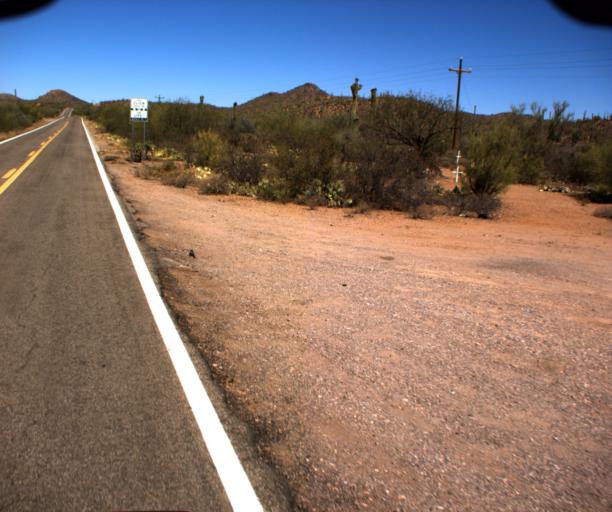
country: US
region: Arizona
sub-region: Pima County
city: Sells
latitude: 32.1687
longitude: -112.1344
